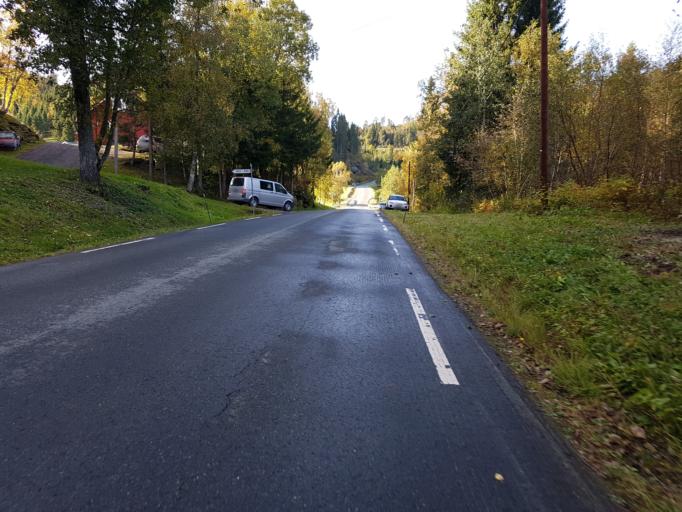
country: NO
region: Sor-Trondelag
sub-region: Klaebu
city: Klaebu
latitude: 63.3447
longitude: 10.5449
